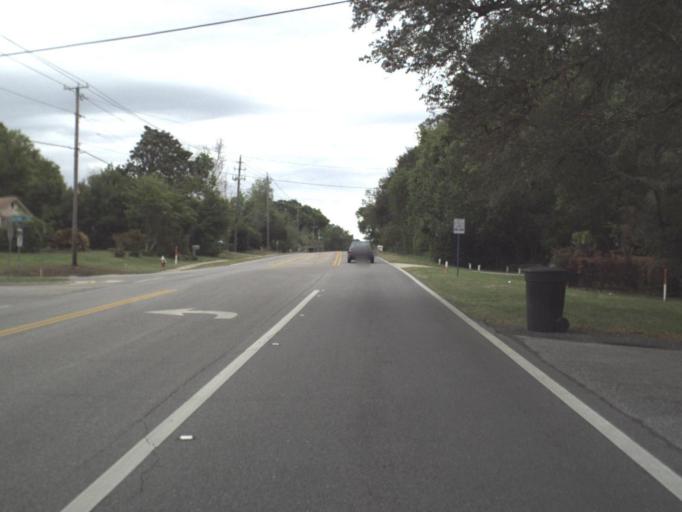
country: US
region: Florida
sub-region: Escambia County
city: East Pensacola Heights
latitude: 30.4503
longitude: -87.1911
